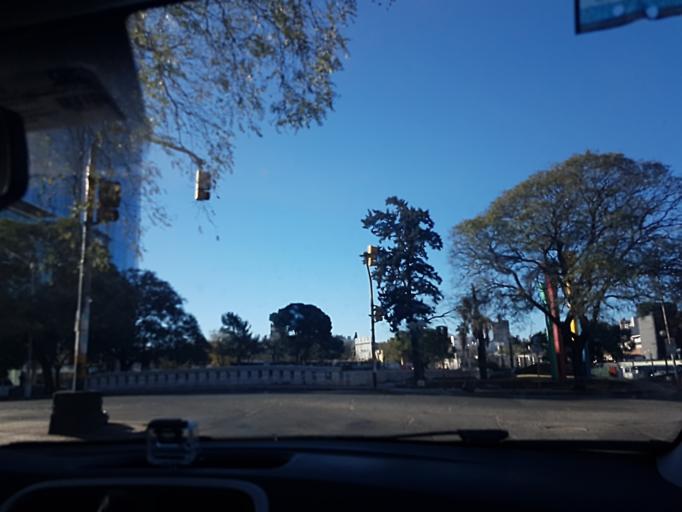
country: AR
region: Cordoba
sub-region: Departamento de Capital
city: Cordoba
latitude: -31.4079
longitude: -64.1898
